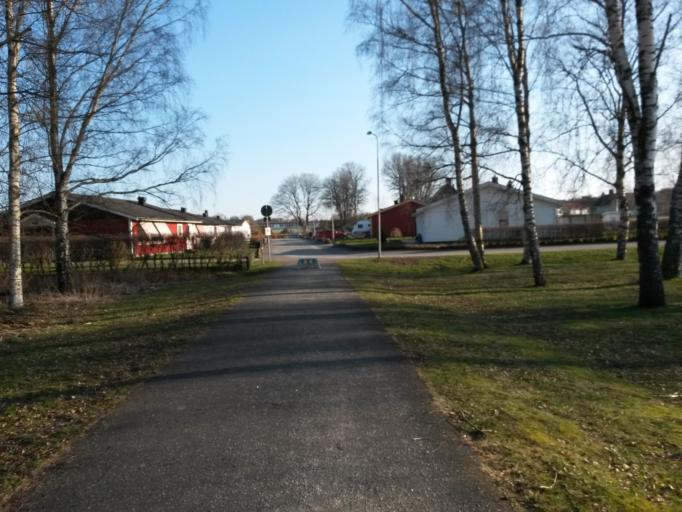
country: SE
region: Vaestra Goetaland
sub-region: Vargarda Kommun
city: Vargarda
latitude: 58.0239
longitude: 12.8138
